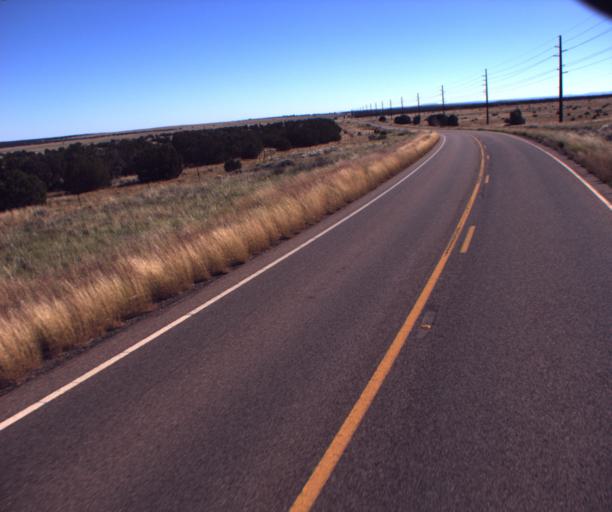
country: US
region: Arizona
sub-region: Navajo County
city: Taylor
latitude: 34.4822
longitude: -110.3035
